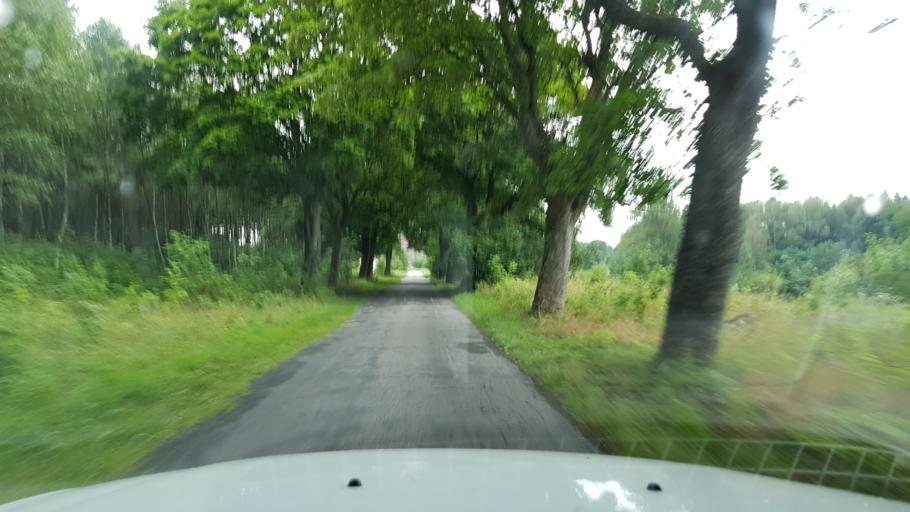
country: PL
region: West Pomeranian Voivodeship
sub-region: Powiat koszalinski
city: Bobolice
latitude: 53.9247
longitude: 16.6576
